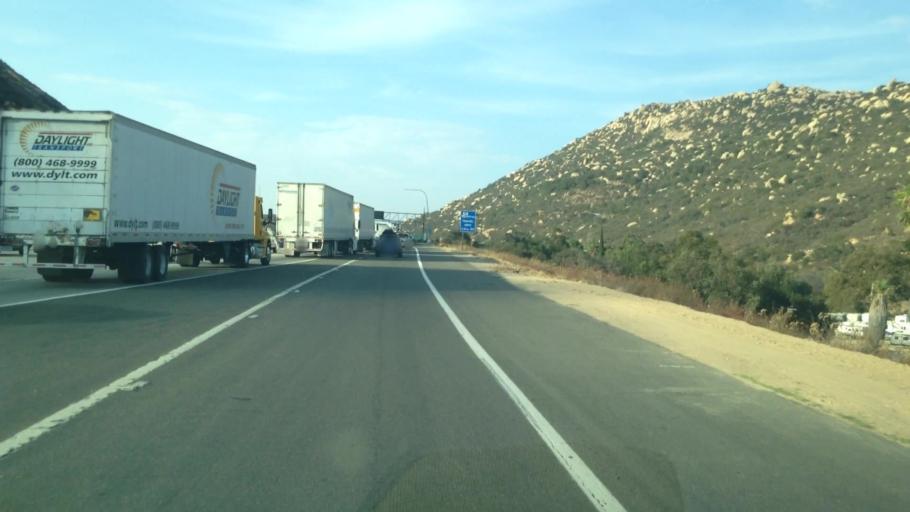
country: US
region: California
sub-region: San Diego County
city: Rainbow
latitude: 33.4336
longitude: -117.1414
